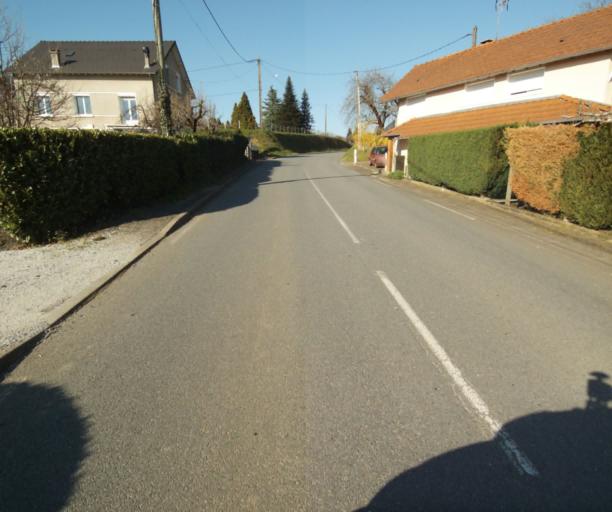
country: FR
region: Limousin
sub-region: Departement de la Correze
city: Saint-Clement
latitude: 45.3391
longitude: 1.6827
